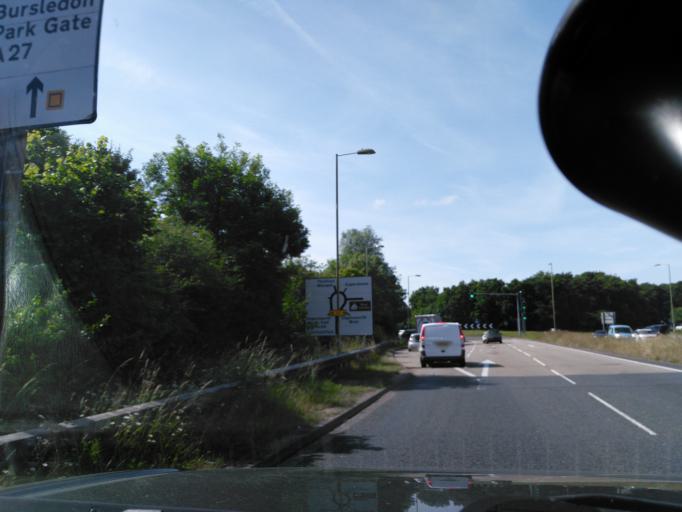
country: GB
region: England
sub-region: Hampshire
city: Botley
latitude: 50.8705
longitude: -1.2541
